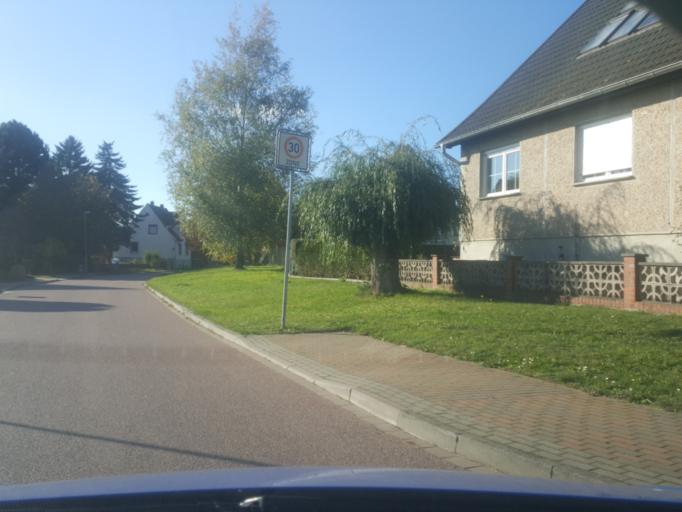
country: DE
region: Saxony-Anhalt
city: Riestedt
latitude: 51.4909
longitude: 11.3657
